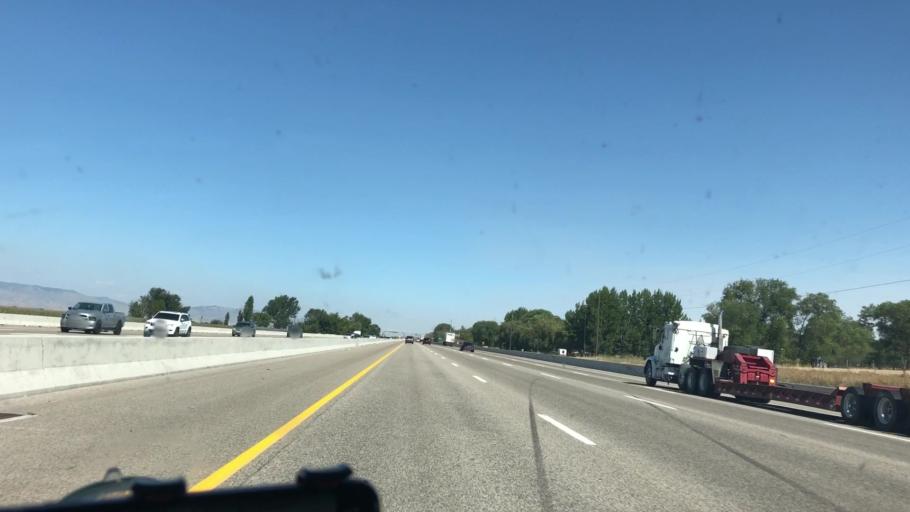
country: US
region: Idaho
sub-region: Ada County
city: Meridian
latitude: 43.5978
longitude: -116.4802
